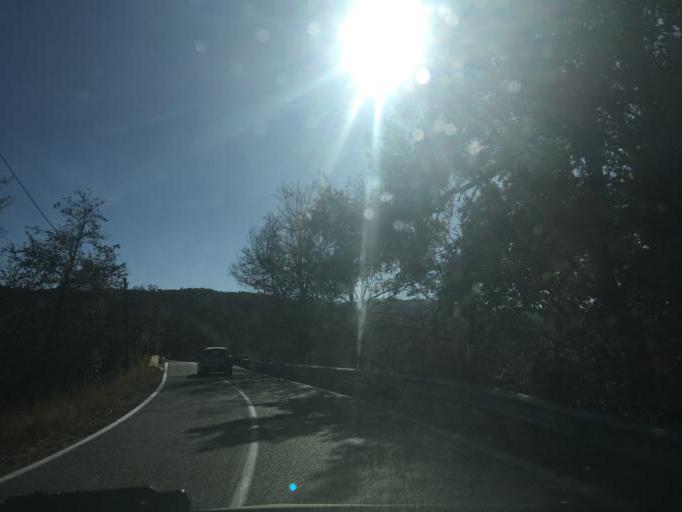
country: FR
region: Provence-Alpes-Cote d'Azur
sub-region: Departement du Var
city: La Garde-Freinet
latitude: 43.3435
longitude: 6.4278
